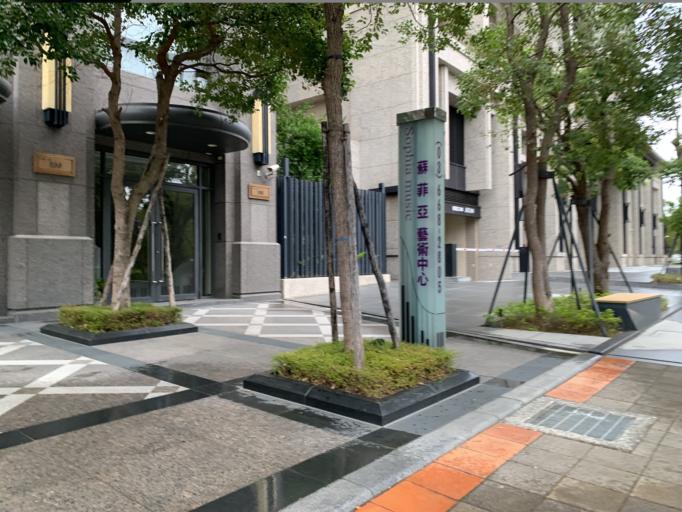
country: TW
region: Taiwan
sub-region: Hsinchu
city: Zhubei
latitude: 24.8153
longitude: 121.0167
